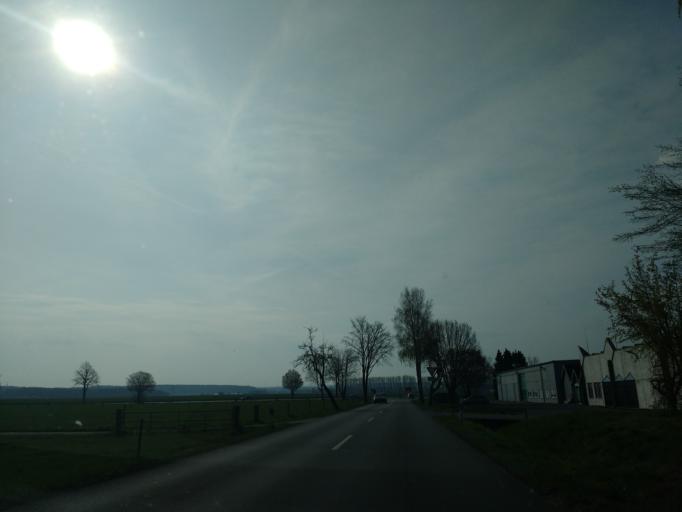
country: DE
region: North Rhine-Westphalia
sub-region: Regierungsbezirk Detmold
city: Salzkotten
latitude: 51.6804
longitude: 8.6270
